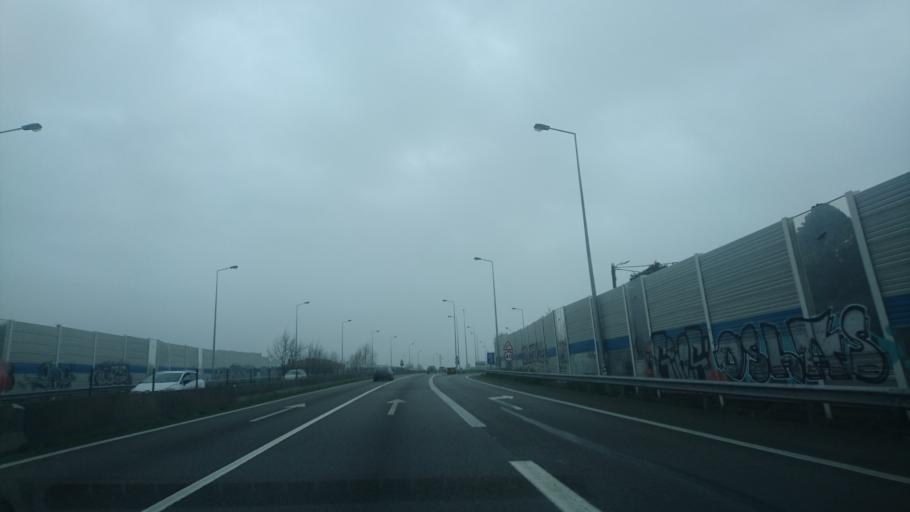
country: PT
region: Porto
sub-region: Vila Nova de Gaia
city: Vilar do Paraiso
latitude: 41.1003
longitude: -8.6267
